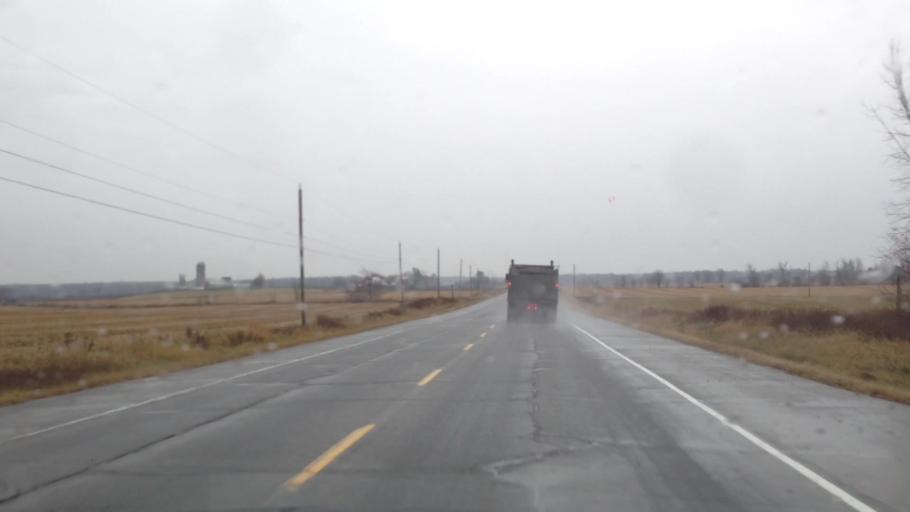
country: CA
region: Ontario
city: Clarence-Rockland
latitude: 45.4122
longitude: -75.4029
